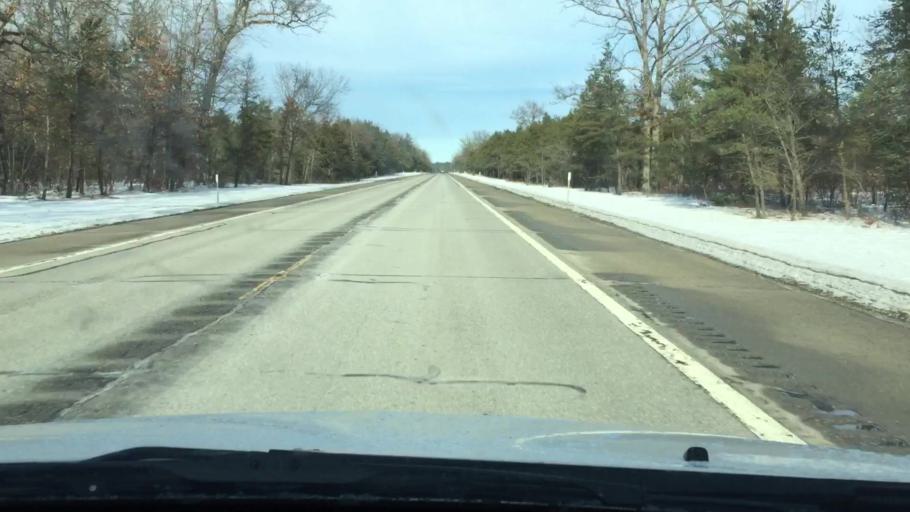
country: US
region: Michigan
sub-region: Wexford County
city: Manton
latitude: 44.5311
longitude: -85.3842
